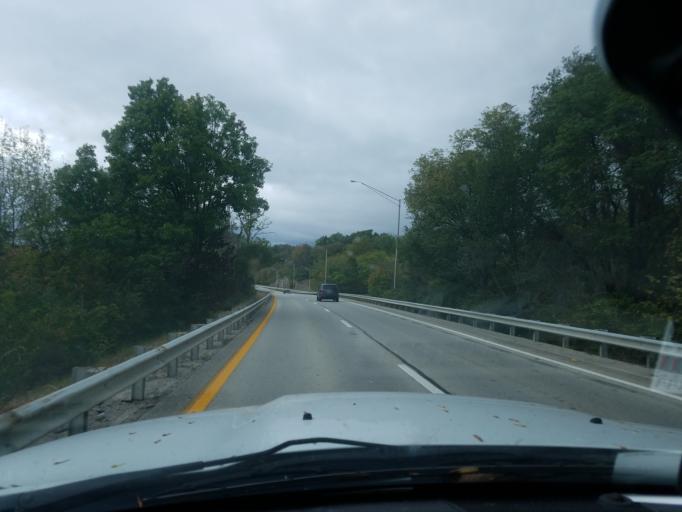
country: US
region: Kentucky
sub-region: Jefferson County
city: Northfield
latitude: 38.2891
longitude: -85.6467
